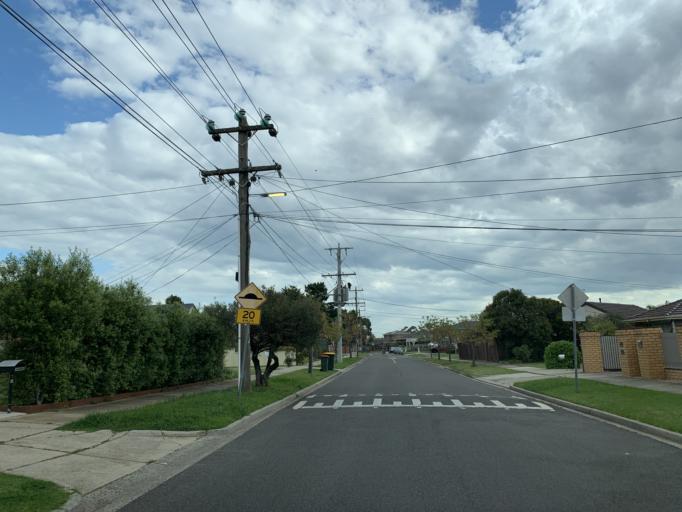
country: AU
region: Victoria
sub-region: Brimbank
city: Albion
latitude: -37.7537
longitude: 144.8527
